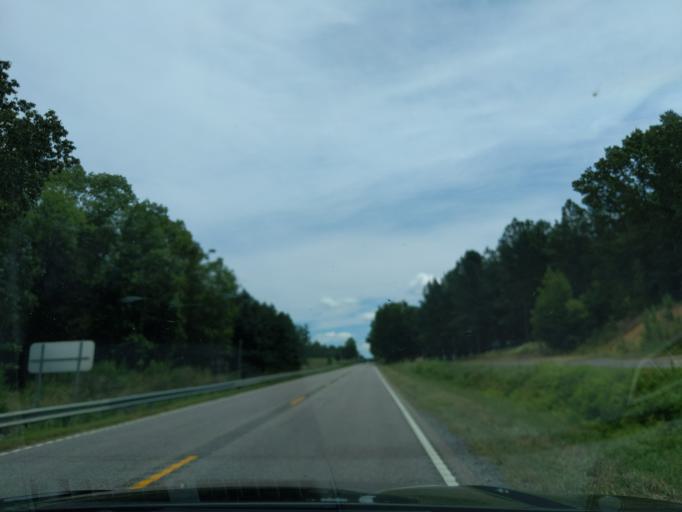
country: US
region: North Carolina
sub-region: Rowan County
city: Rockwell
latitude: 35.4583
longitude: -80.3286
